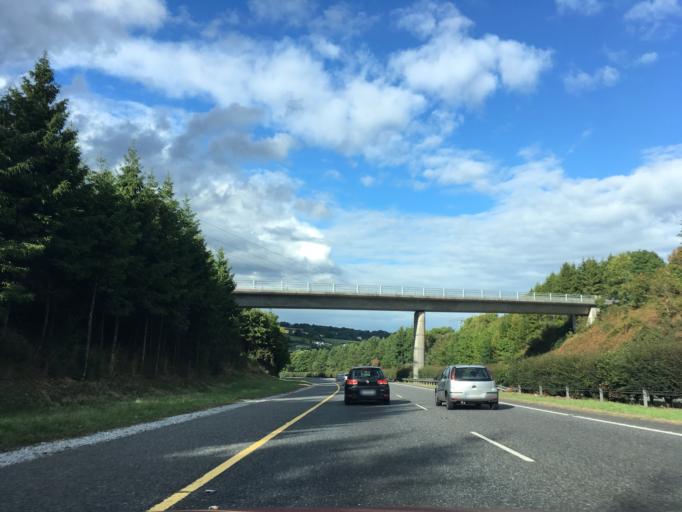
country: IE
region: Munster
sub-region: County Cork
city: Passage West
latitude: 51.9265
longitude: -8.3777
